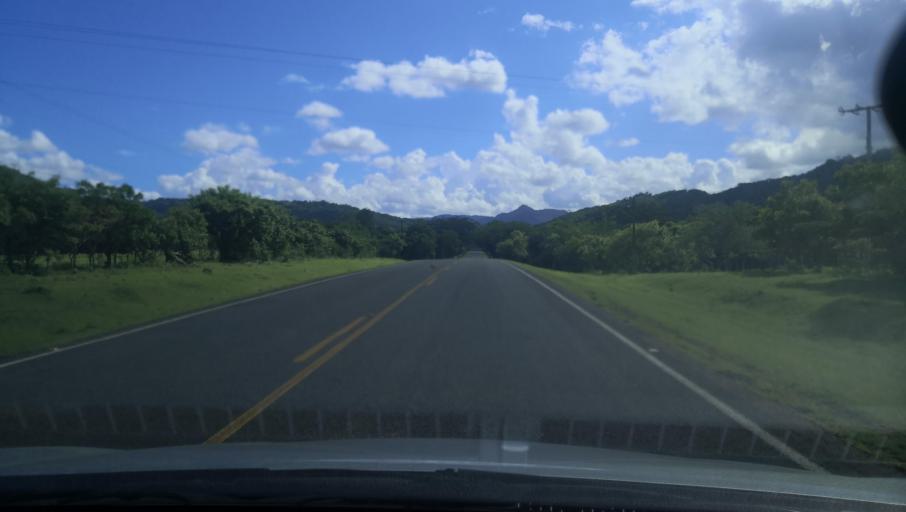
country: NI
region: Madriz
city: Somoto
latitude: 13.4592
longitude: -86.6661
